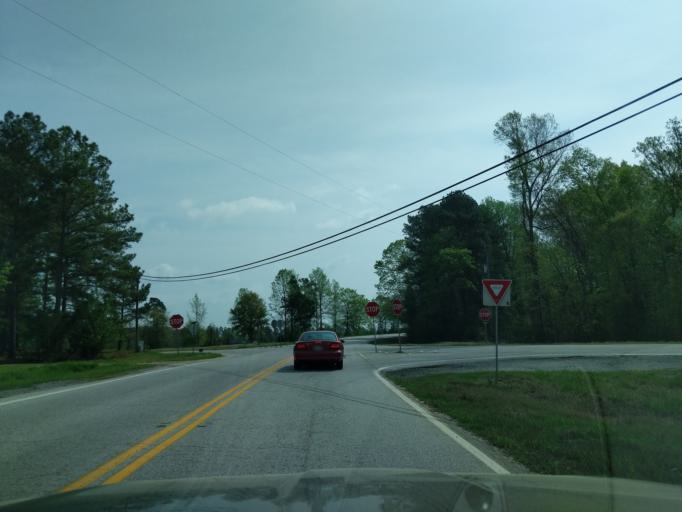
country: US
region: Georgia
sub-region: Lincoln County
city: Lincolnton
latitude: 33.8057
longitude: -82.3972
